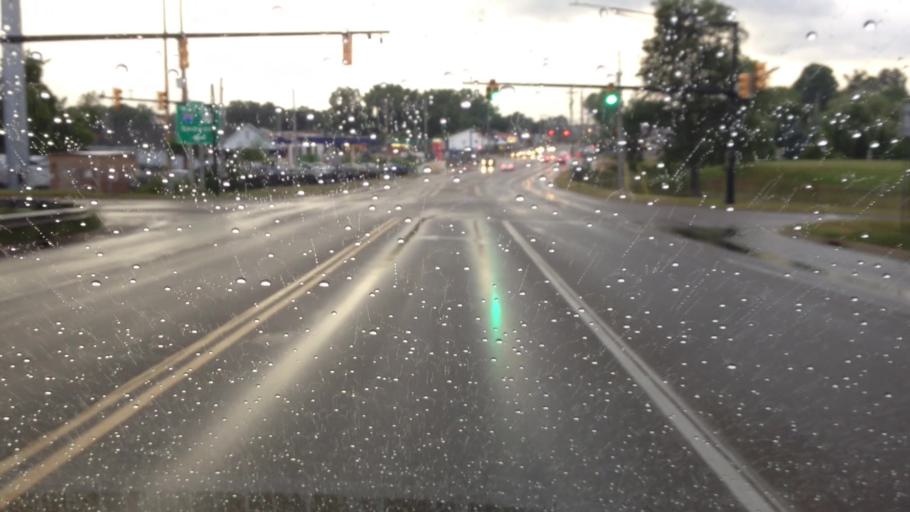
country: US
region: Ohio
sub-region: Summit County
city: Portage Lakes
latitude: 41.0265
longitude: -81.5268
